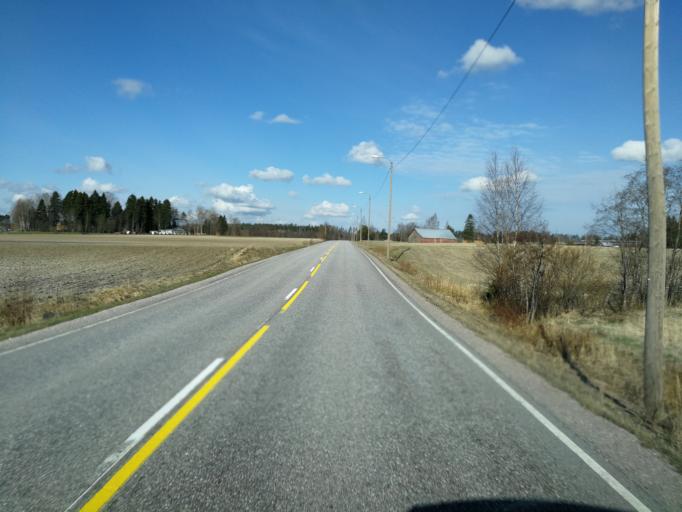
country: FI
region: Uusimaa
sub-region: Helsinki
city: Kirkkonummi
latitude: 60.2021
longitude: 24.3849
